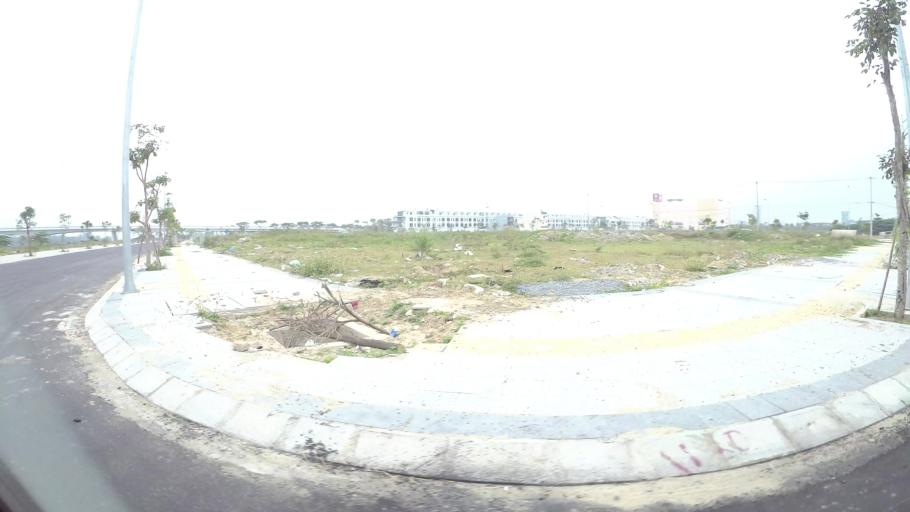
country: VN
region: Da Nang
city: Son Tra
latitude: 16.0375
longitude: 108.2339
